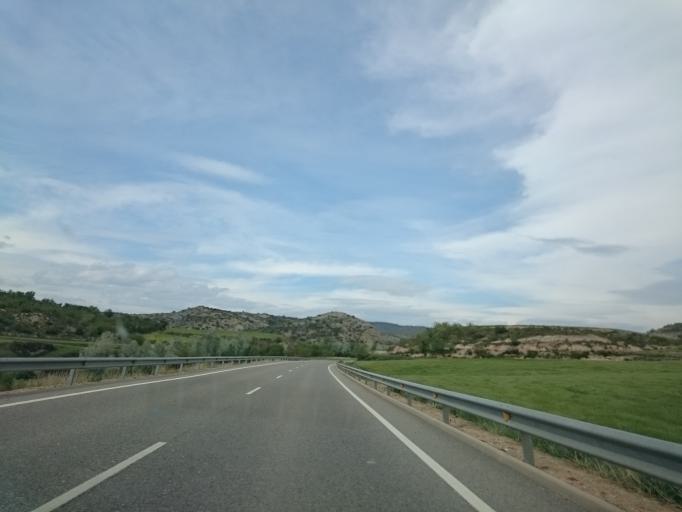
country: ES
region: Catalonia
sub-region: Provincia de Lleida
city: Tora de Riubregos
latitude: 41.8204
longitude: 1.3247
